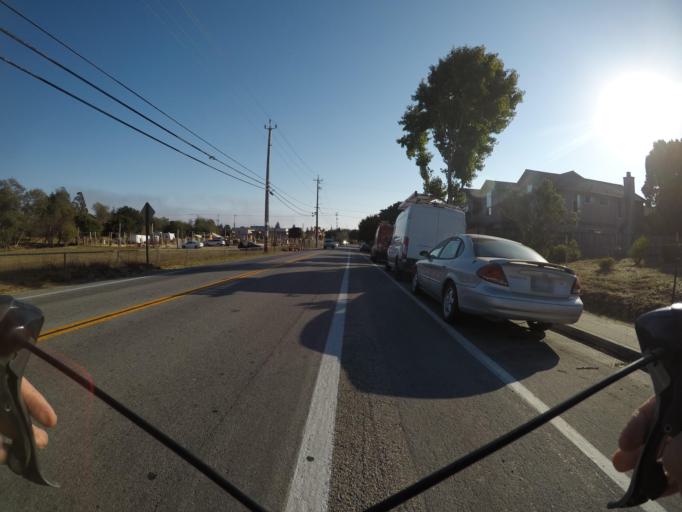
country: US
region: California
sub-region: Santa Cruz County
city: Live Oak
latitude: 36.9900
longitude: -121.9788
